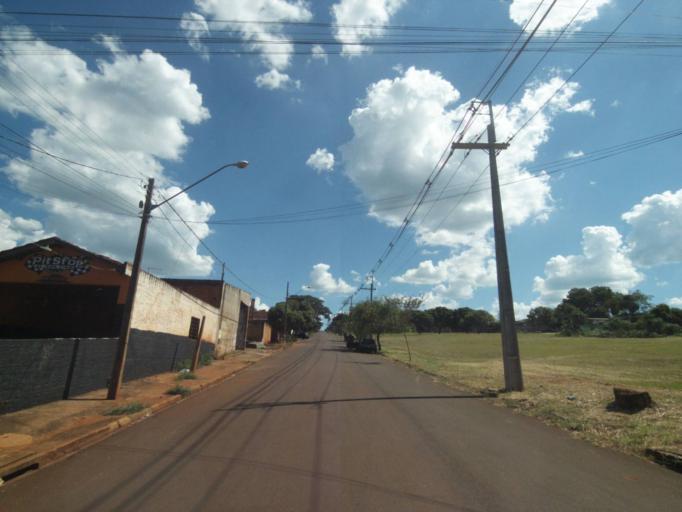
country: BR
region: Parana
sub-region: Sertanopolis
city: Sertanopolis
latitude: -23.0395
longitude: -50.8215
